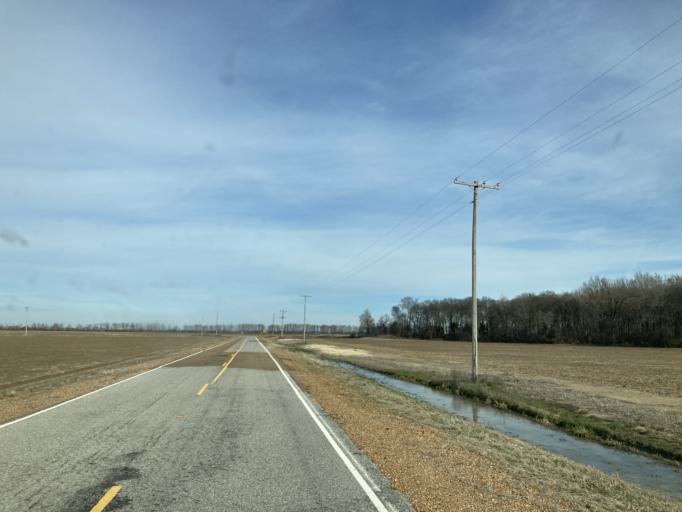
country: US
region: Mississippi
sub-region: Humphreys County
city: Belzoni
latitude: 33.0604
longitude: -90.6303
